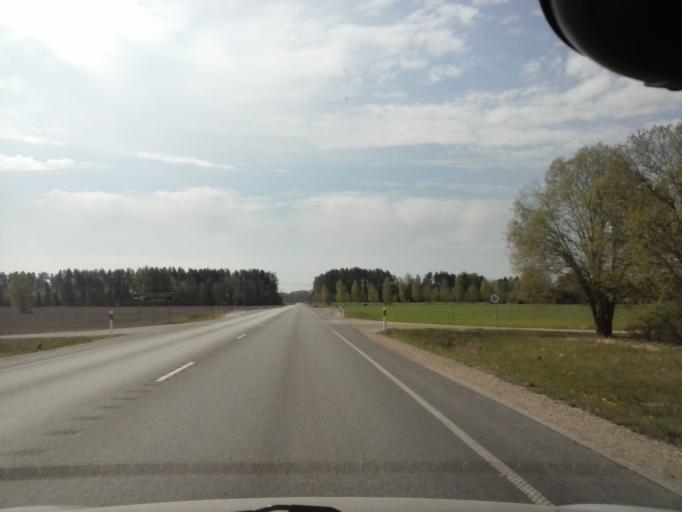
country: EE
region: Tartu
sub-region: UElenurme vald
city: Ulenurme
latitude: 58.2186
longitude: 26.7031
